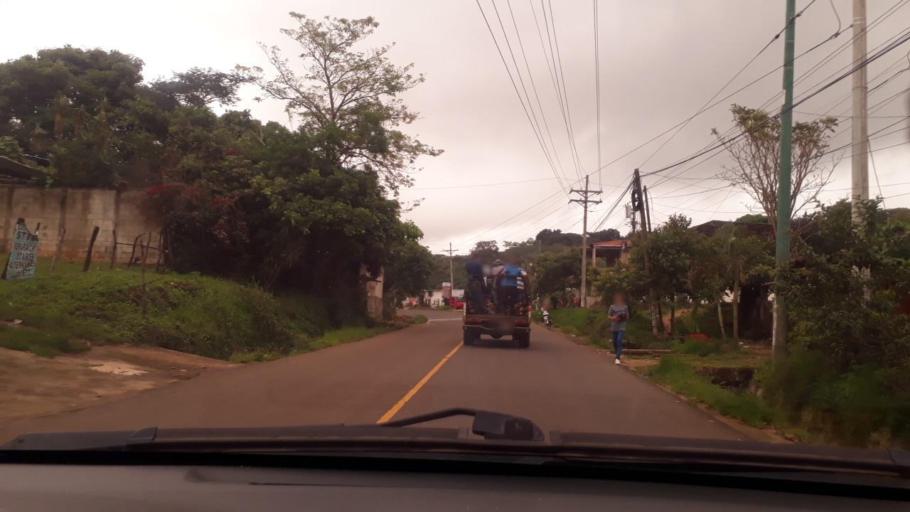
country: GT
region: Jutiapa
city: Moyuta
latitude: 14.0445
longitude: -90.0679
